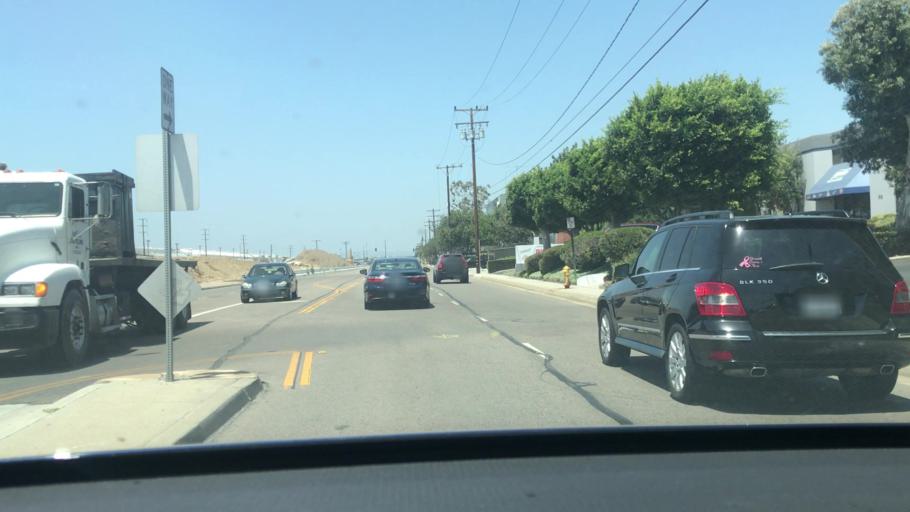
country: US
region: California
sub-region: Los Angeles County
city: Del Aire
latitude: 33.9172
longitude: -118.3783
